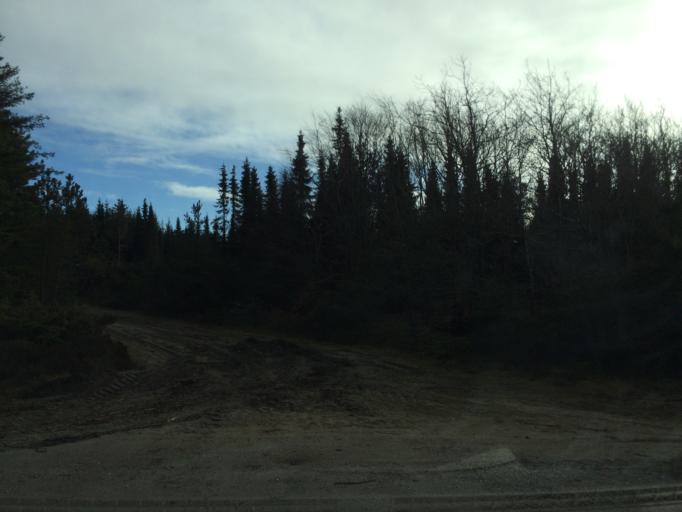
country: DK
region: Central Jutland
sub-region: Holstebro Kommune
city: Ulfborg
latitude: 56.2574
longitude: 8.4268
